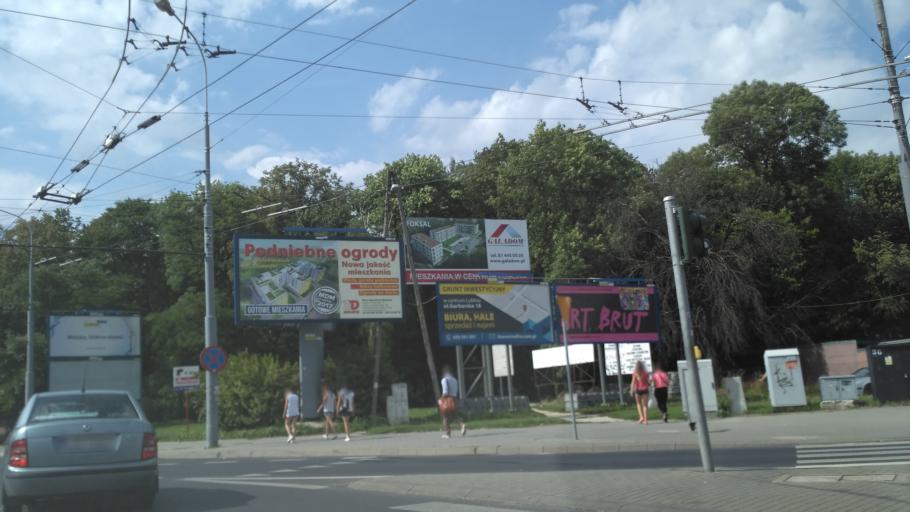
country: PL
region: Lublin Voivodeship
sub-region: Powiat lubelski
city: Lublin
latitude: 51.2365
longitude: 22.5767
